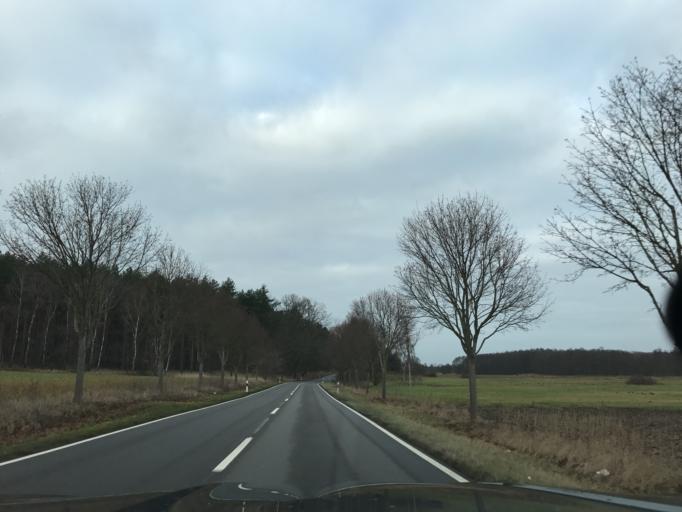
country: DE
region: Brandenburg
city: Brandenburg an der Havel
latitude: 52.3552
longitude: 12.6085
